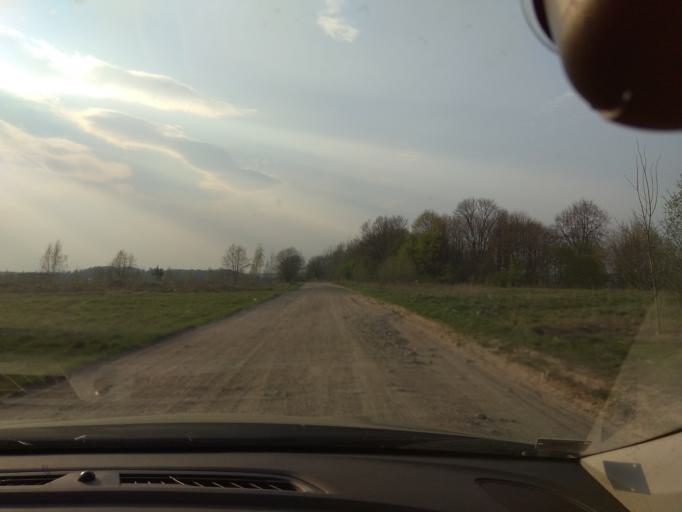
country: LT
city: Baltoji Voke
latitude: 54.5930
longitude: 25.1692
